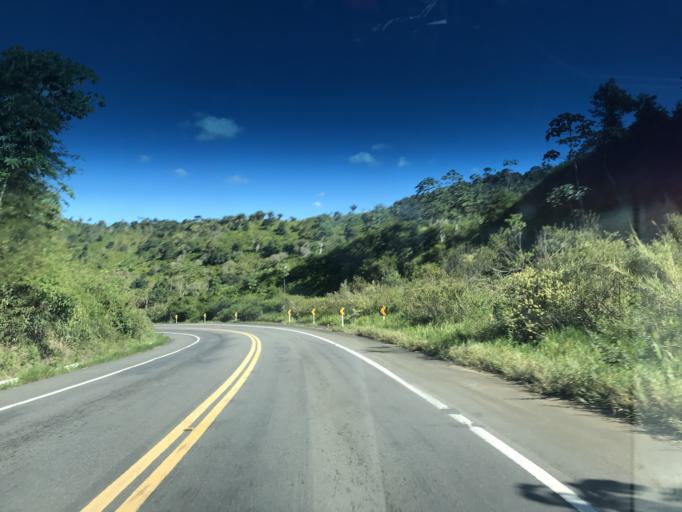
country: BR
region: Bahia
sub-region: Gandu
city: Gandu
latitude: -13.8807
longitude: -39.4886
